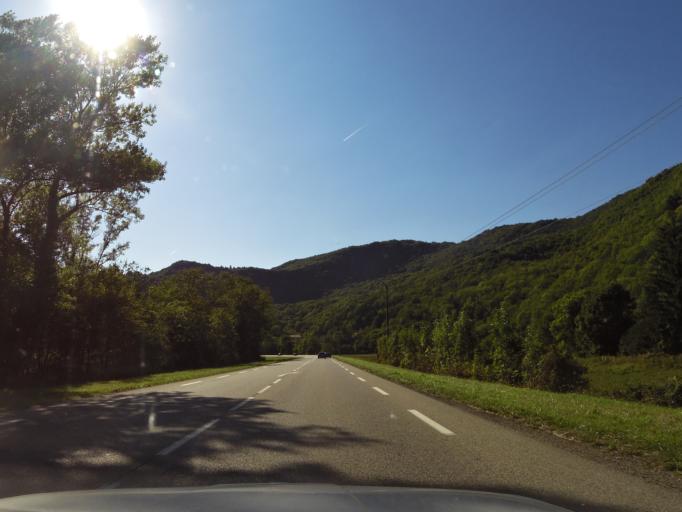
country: FR
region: Rhone-Alpes
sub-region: Departement de l'Ain
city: Saint-Rambert-en-Bugey
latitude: 45.9358
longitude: 5.4174
